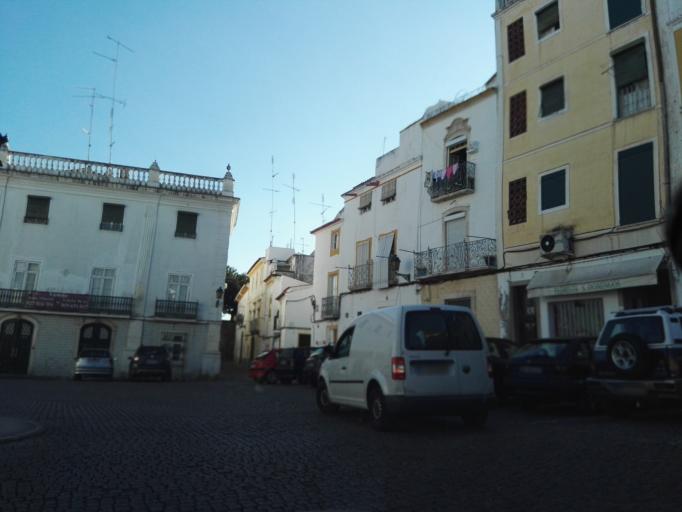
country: PT
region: Portalegre
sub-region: Elvas
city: Elvas
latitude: 38.8793
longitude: -7.1606
